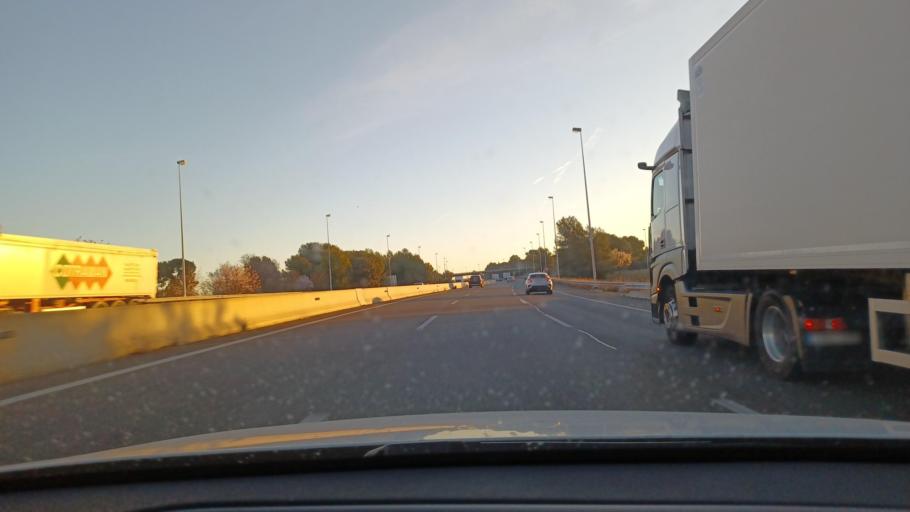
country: ES
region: Catalonia
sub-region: Provincia de Tarragona
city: Santa Oliva
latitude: 41.2688
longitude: 1.5474
